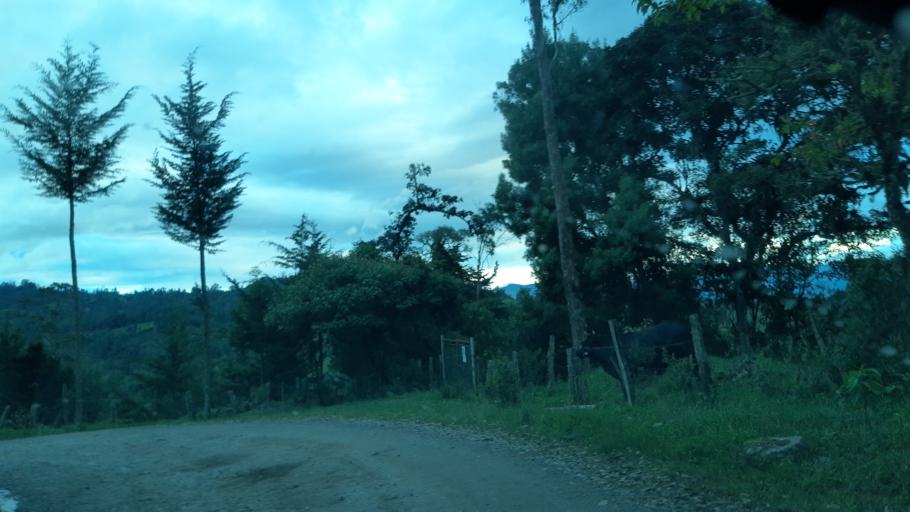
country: CO
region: Boyaca
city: Garagoa
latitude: 5.0937
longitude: -73.3352
